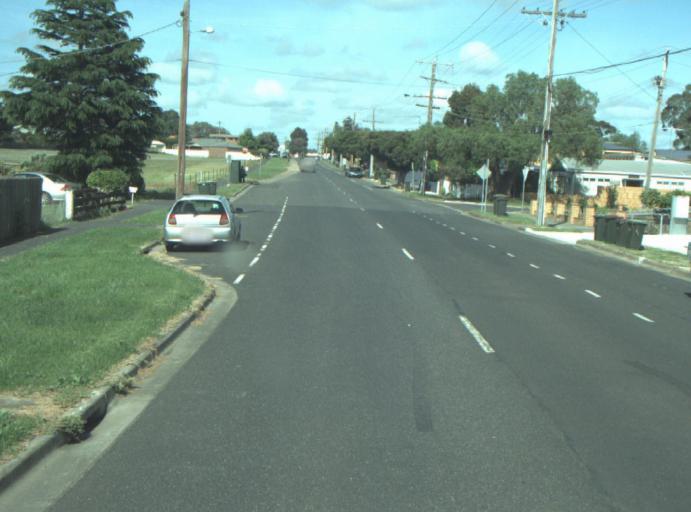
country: AU
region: Victoria
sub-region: Greater Geelong
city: Lara
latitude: -38.0205
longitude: 144.4007
